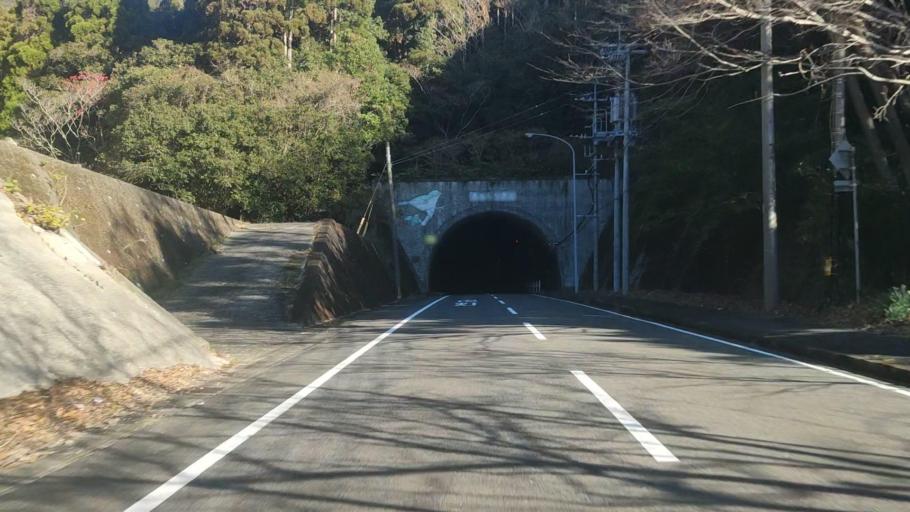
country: JP
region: Miyazaki
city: Nobeoka
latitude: 32.6910
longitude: 131.8100
